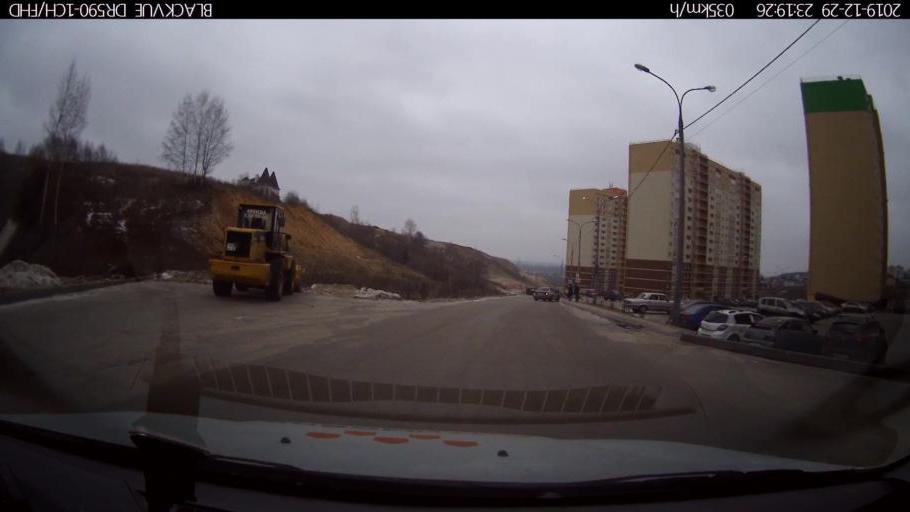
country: RU
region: Nizjnij Novgorod
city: Afonino
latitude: 56.2820
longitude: 44.0882
